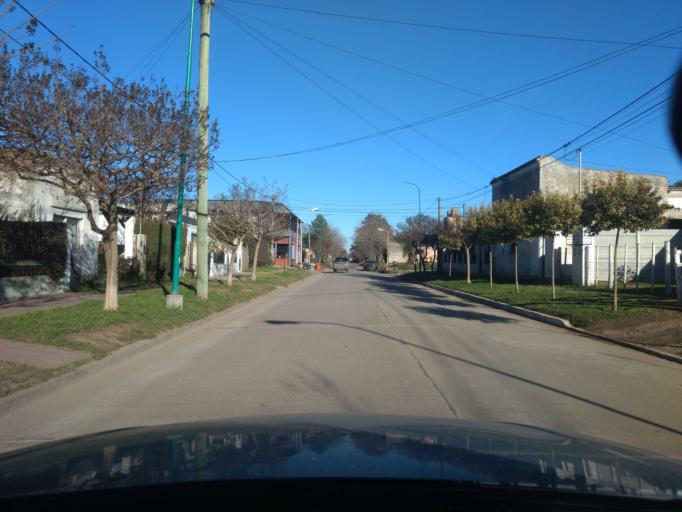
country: AR
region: Buenos Aires
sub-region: Partido de Navarro
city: Navarro
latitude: -34.9997
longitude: -59.2740
